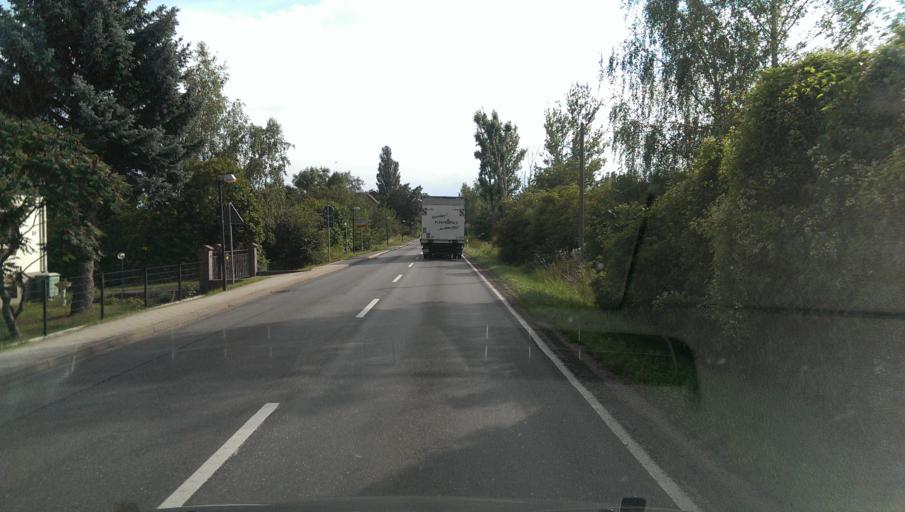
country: DE
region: Saxony
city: Elstertrebnitz
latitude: 51.1056
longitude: 12.1864
